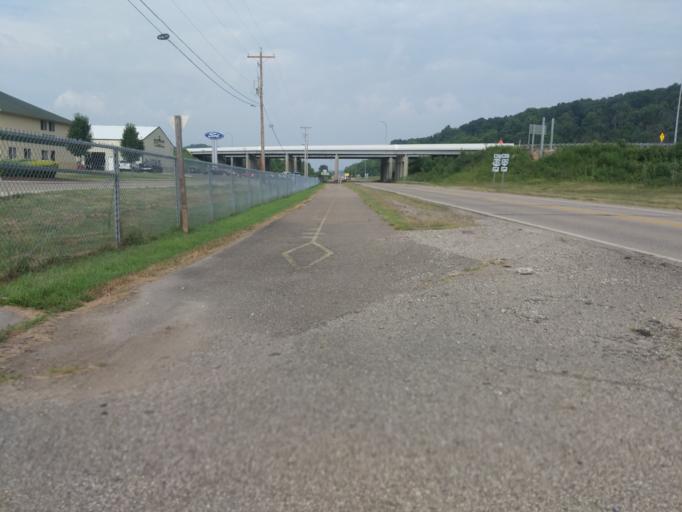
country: US
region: Ohio
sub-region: Athens County
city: Athens
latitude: 39.3343
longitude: -82.0326
